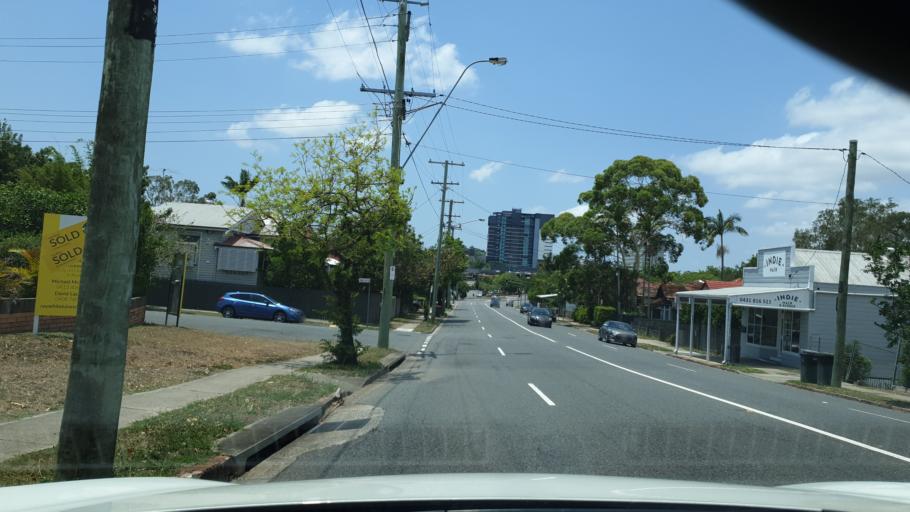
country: AU
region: Queensland
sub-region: Brisbane
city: Wooloowin
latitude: -27.4289
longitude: 153.0352
